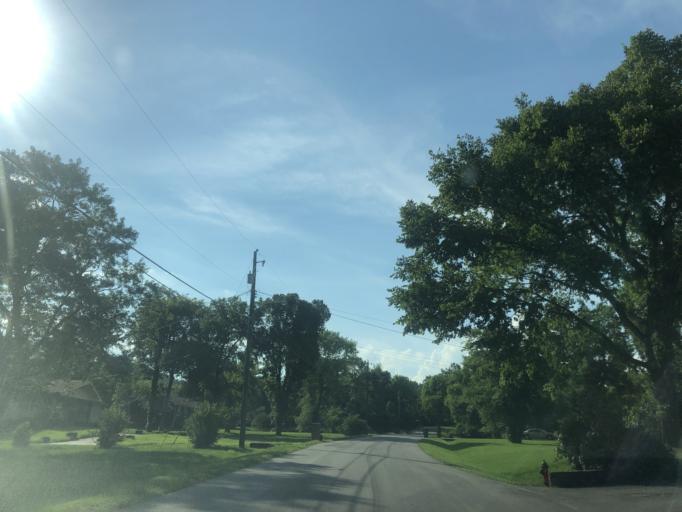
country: US
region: Tennessee
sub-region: Davidson County
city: Nashville
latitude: 36.2413
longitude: -86.8349
